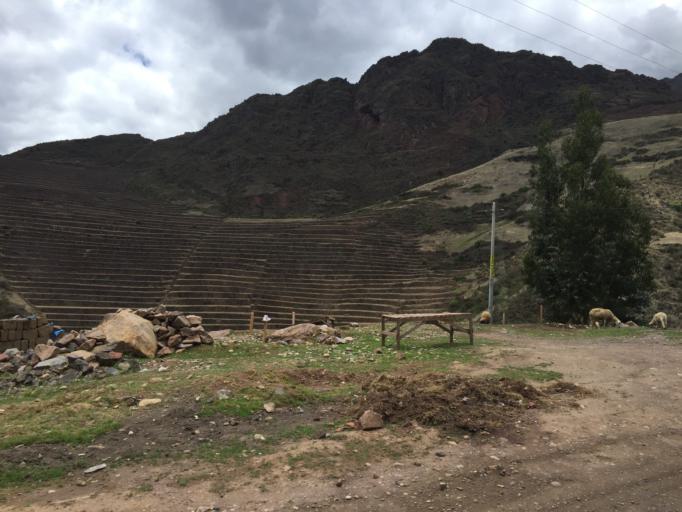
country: PE
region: Cusco
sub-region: Provincia de Calca
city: Pisac
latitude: -13.4117
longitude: -71.8368
